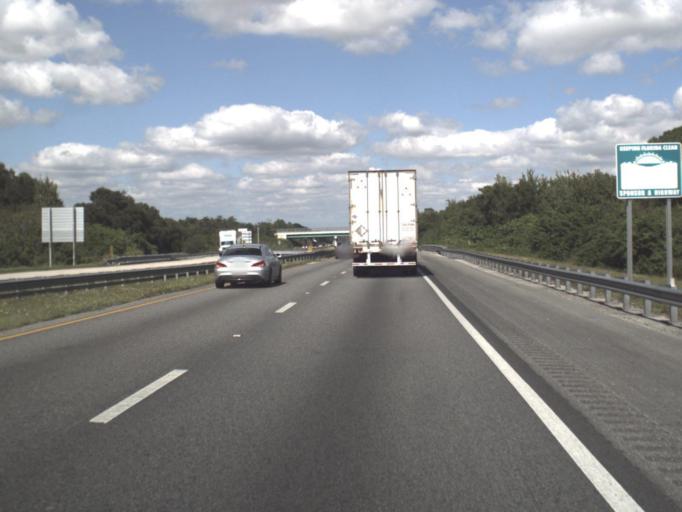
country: US
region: Florida
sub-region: Osceola County
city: Buenaventura Lakes
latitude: 28.3005
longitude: -81.3586
